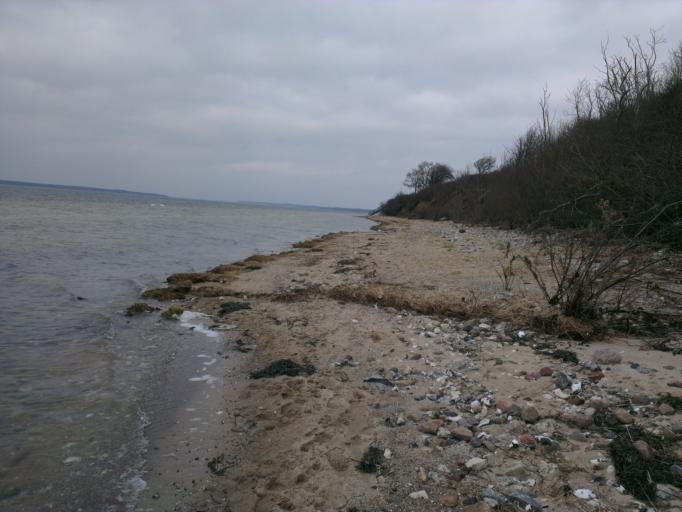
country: DK
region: Capital Region
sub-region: Frederikssund Kommune
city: Frederikssund
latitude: 55.8540
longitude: 12.0450
